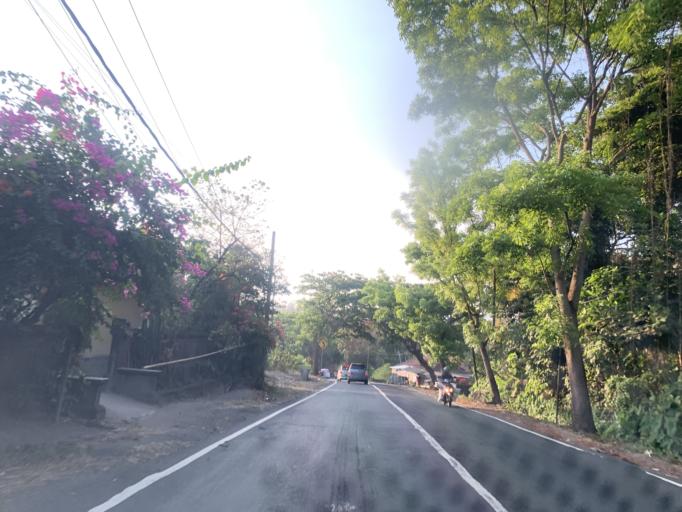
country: ID
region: Bali
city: Banjar Delodrurung
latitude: -8.5002
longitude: 114.9694
